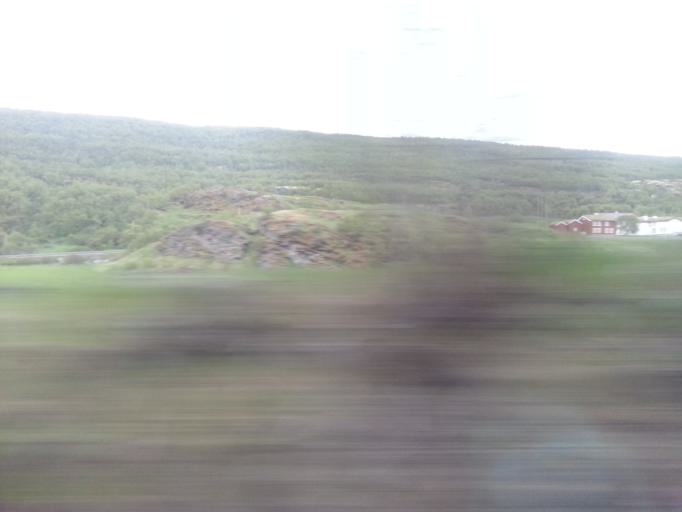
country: NO
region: Sor-Trondelag
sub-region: Oppdal
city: Oppdal
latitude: 62.3055
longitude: 9.6032
